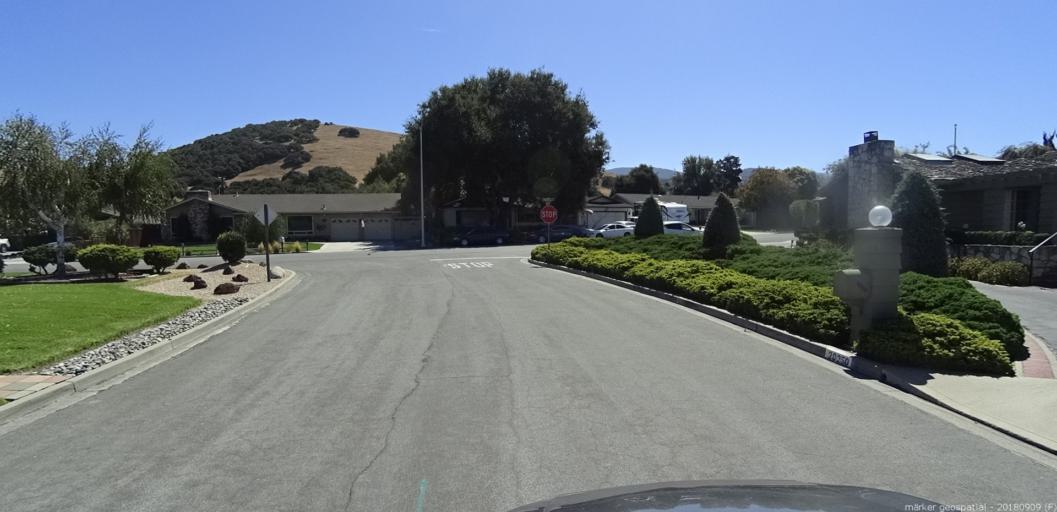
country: US
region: California
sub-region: Monterey County
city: Salinas
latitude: 36.6102
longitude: -121.6926
